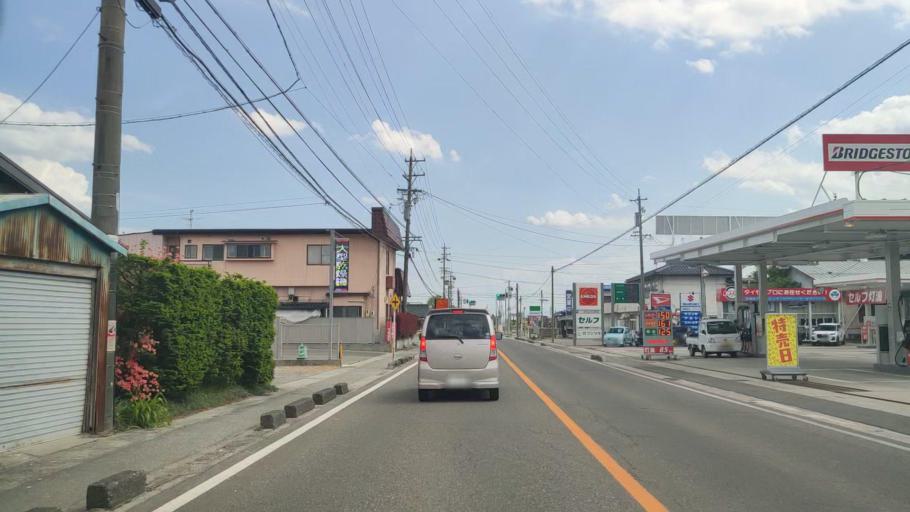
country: JP
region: Nagano
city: Omachi
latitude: 36.4694
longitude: 137.8489
